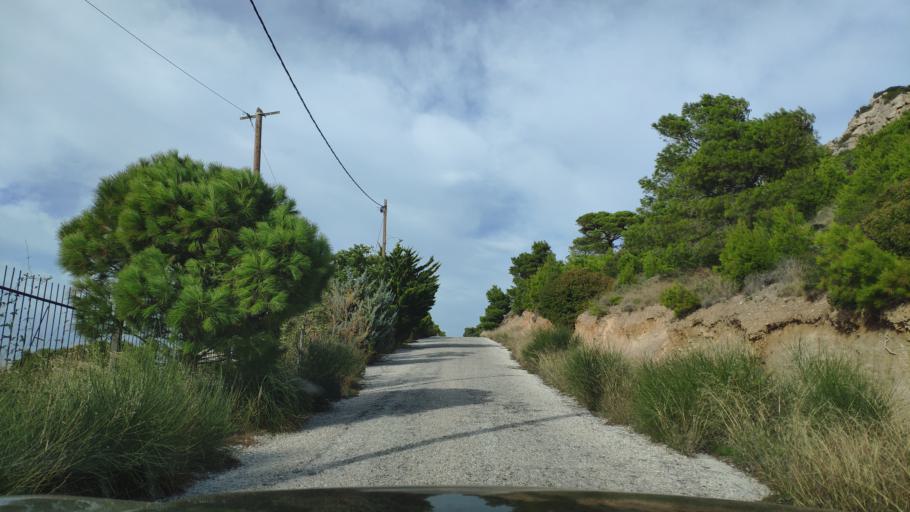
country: GR
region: Attica
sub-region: Nomarchia Anatolikis Attikis
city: Limin Mesoyaias
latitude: 37.9088
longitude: 24.0199
